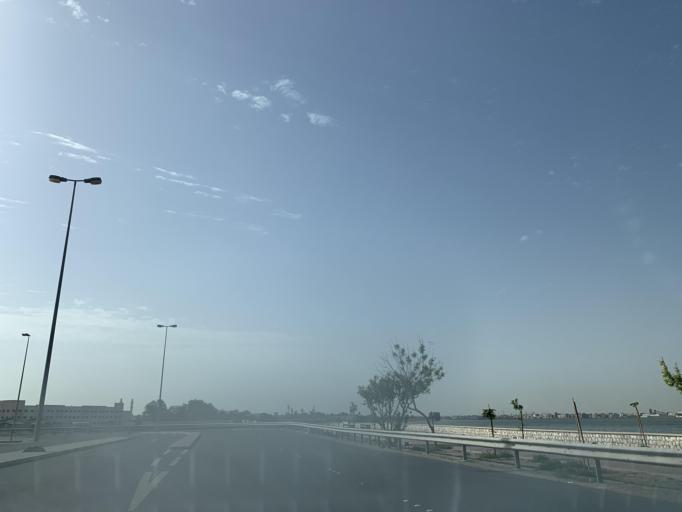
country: BH
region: Northern
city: Sitrah
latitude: 26.1683
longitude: 50.5995
